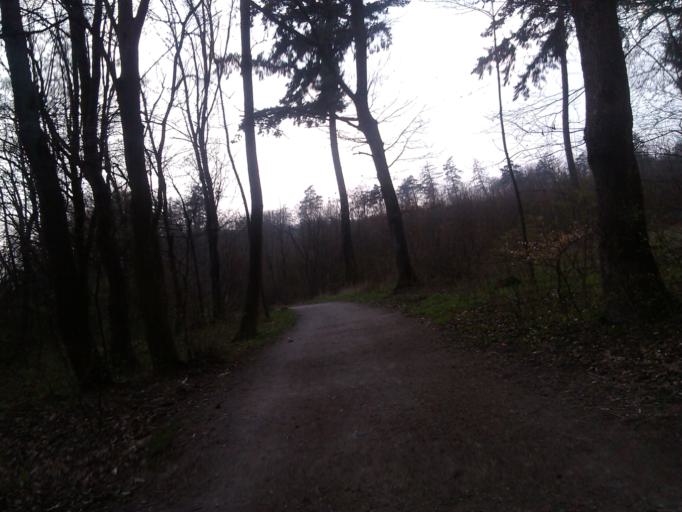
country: CZ
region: South Moravian
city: Bilovice nad Svitavou
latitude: 49.2250
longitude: 16.6878
